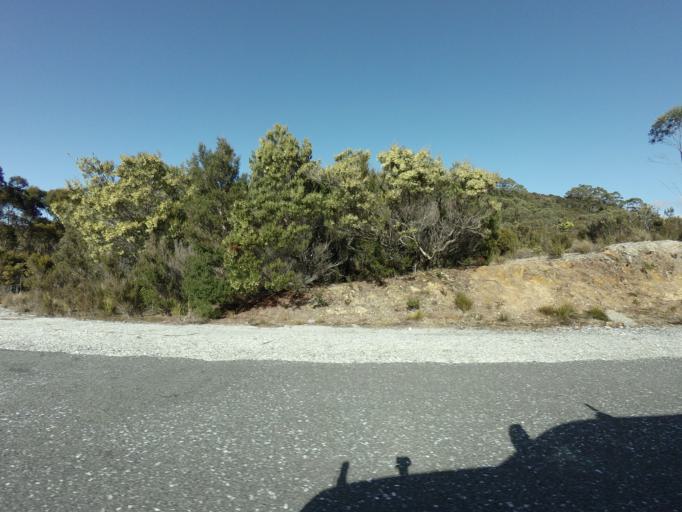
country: AU
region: Tasmania
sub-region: West Coast
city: Queenstown
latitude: -42.7923
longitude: 146.0640
